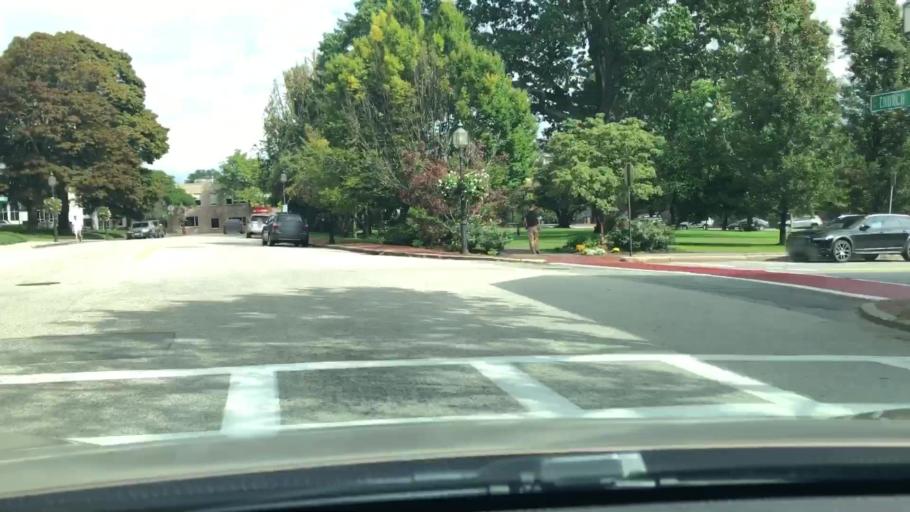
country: US
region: Massachusetts
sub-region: Middlesex County
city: Winchester
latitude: 42.4516
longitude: -71.1387
